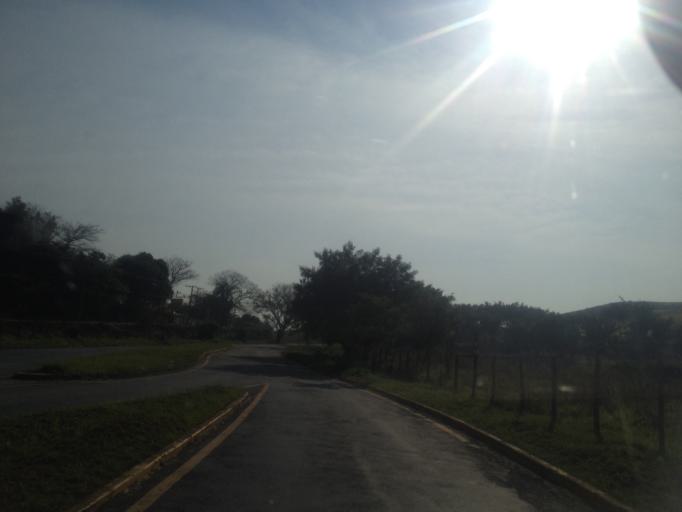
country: BR
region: Rio de Janeiro
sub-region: Porto Real
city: Porto Real
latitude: -22.4473
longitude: -44.3212
